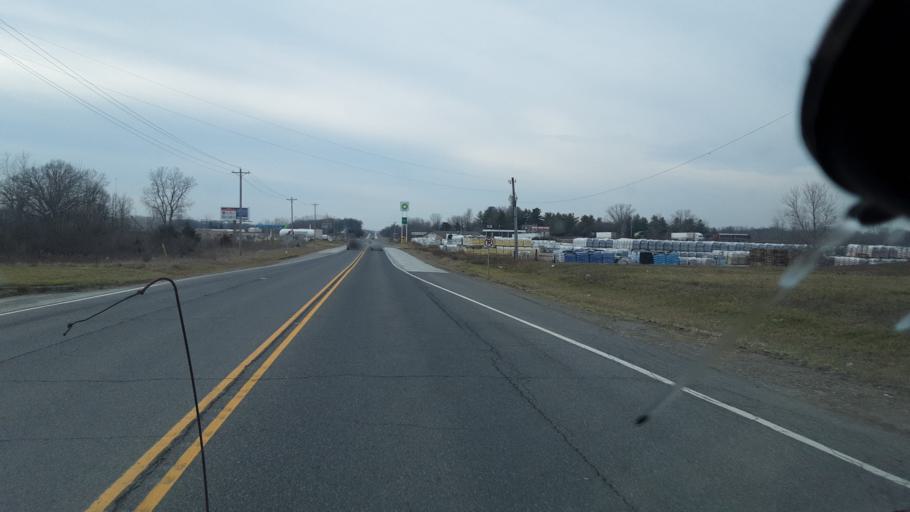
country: US
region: Indiana
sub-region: DeKalb County
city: Waterloo
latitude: 41.4396
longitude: -85.0577
